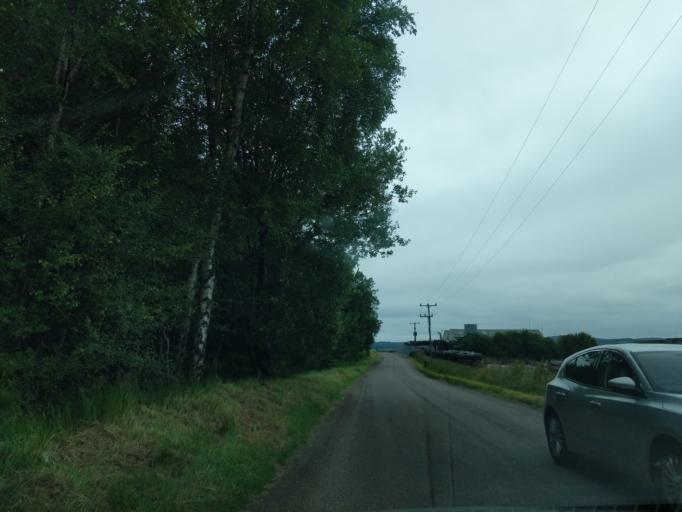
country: GB
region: Scotland
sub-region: Moray
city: Rothes
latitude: 57.4802
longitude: -3.1775
